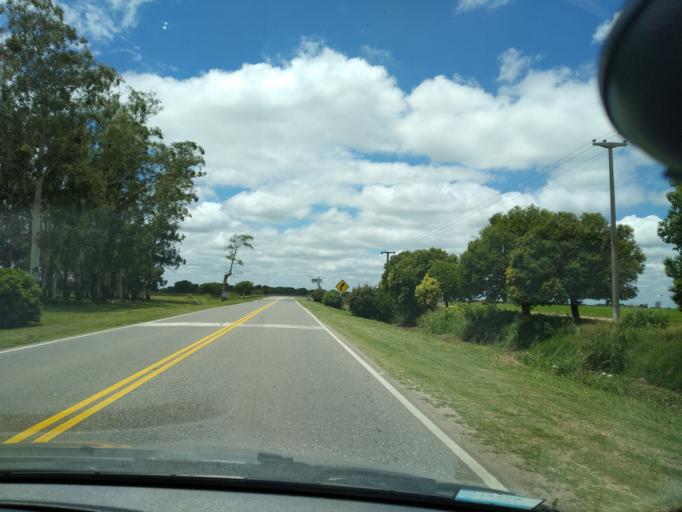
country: AR
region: Cordoba
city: Toledo
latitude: -31.6484
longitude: -64.0840
